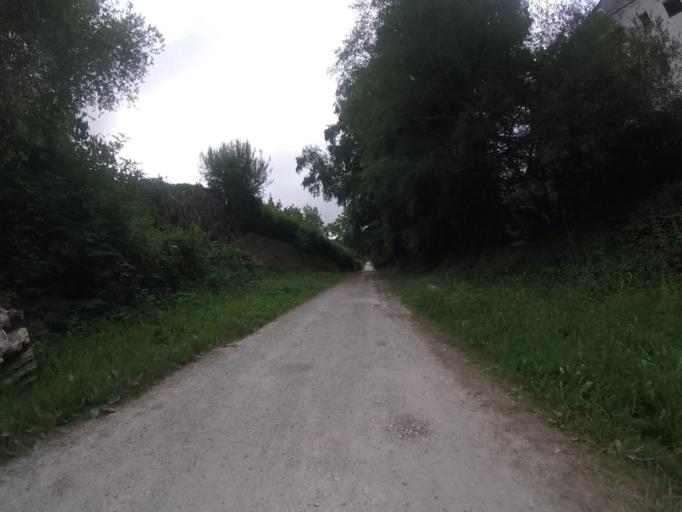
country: ES
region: Navarre
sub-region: Provincia de Navarra
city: Leitza
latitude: 43.0867
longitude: -1.9165
